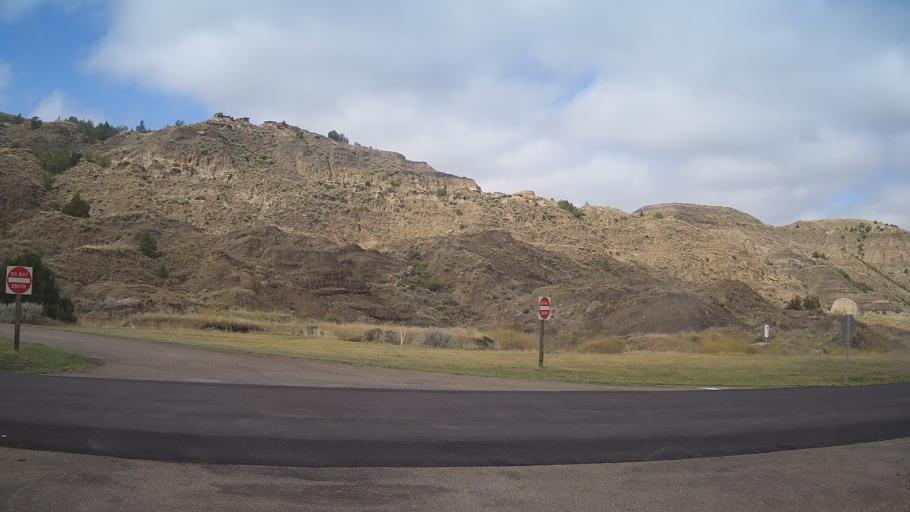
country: US
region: Montana
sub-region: Dawson County
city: Glendive
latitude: 47.0763
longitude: -104.6955
